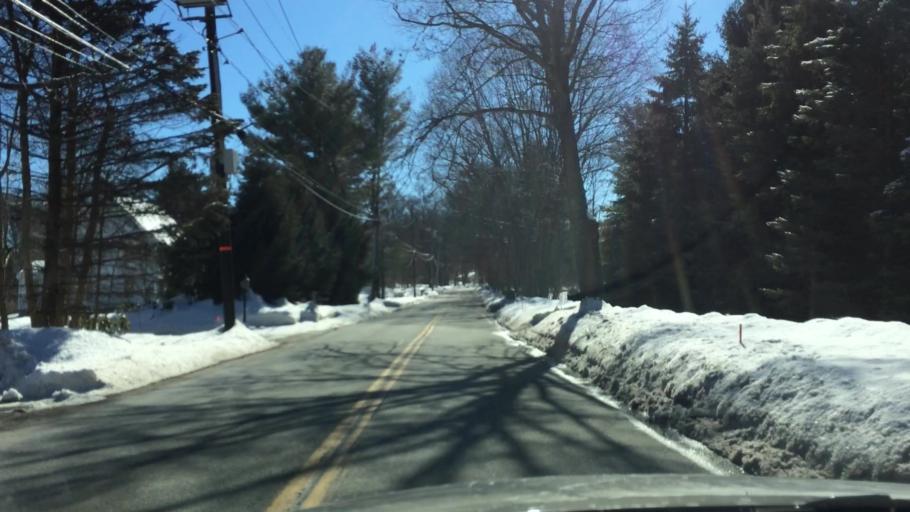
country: US
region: Massachusetts
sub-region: Middlesex County
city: Bedford
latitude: 42.5146
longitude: -71.2585
